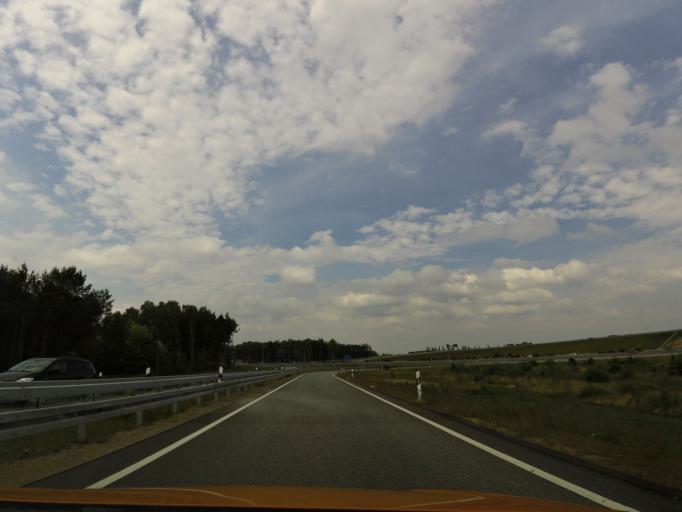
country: DE
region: Mecklenburg-Vorpommern
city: Gross Laasch
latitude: 53.4229
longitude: 11.5186
